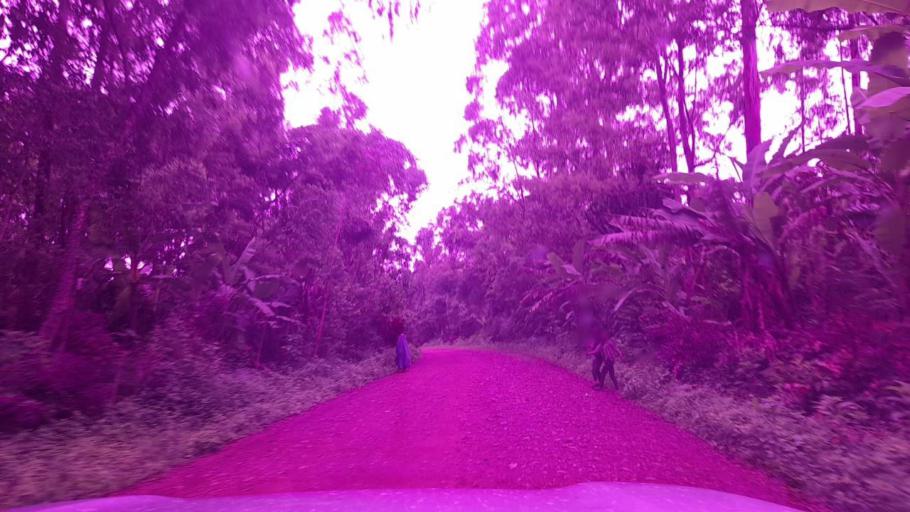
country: ET
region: Southern Nations, Nationalities, and People's Region
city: Bonga
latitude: 7.5795
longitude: 36.0234
